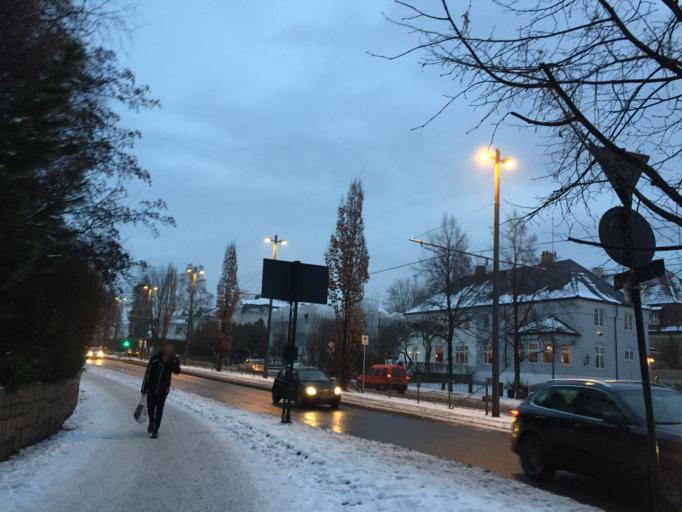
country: NO
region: Oslo
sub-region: Oslo
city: Sjolyststranda
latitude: 59.9228
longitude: 10.7046
